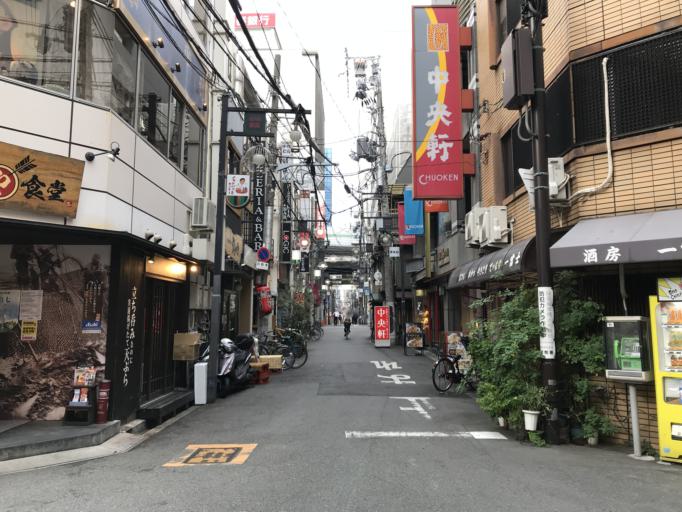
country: JP
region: Osaka
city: Osaka-shi
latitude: 34.6662
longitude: 135.4994
